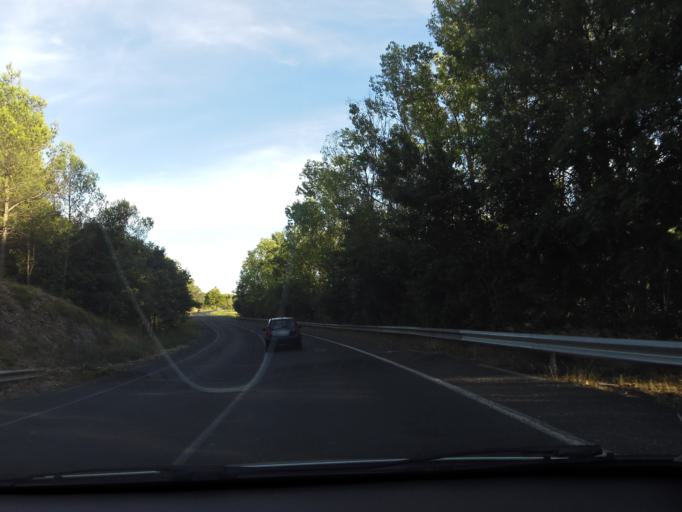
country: FR
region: Languedoc-Roussillon
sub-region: Departement de l'Herault
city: Montferrier-sur-Lez
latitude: 43.6603
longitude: 3.8664
